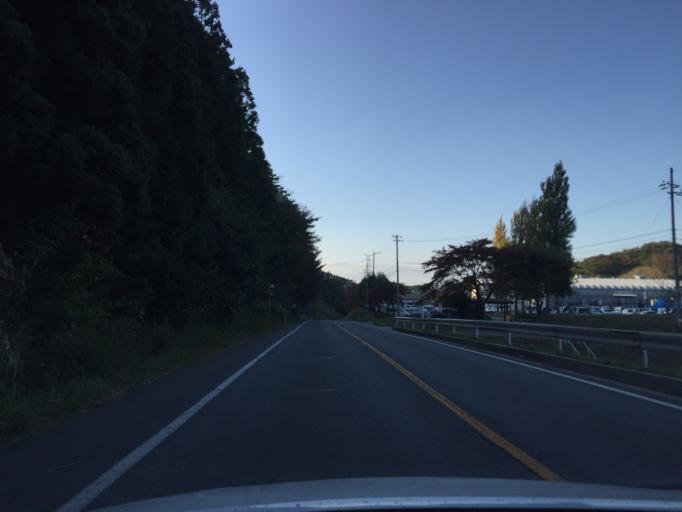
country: JP
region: Fukushima
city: Ishikawa
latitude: 37.1724
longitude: 140.6527
